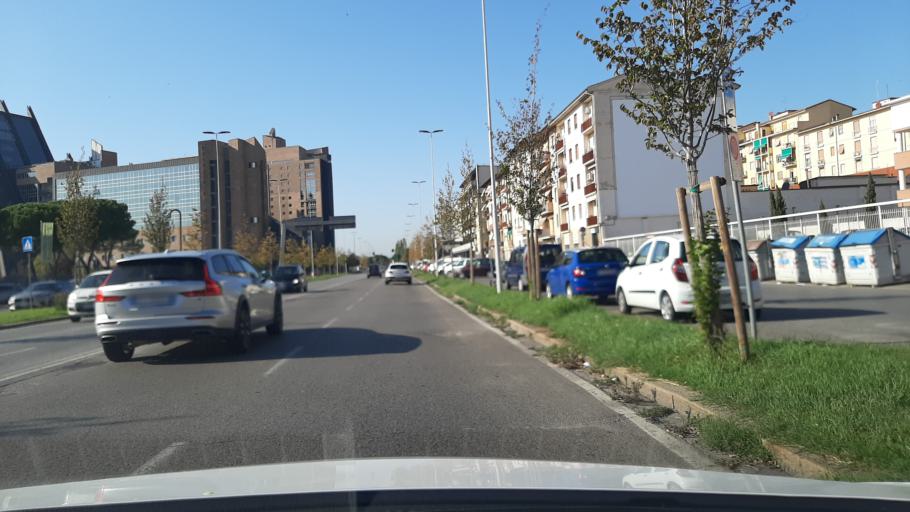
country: IT
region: Tuscany
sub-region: Province of Florence
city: Florence
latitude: 43.7950
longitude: 11.2297
